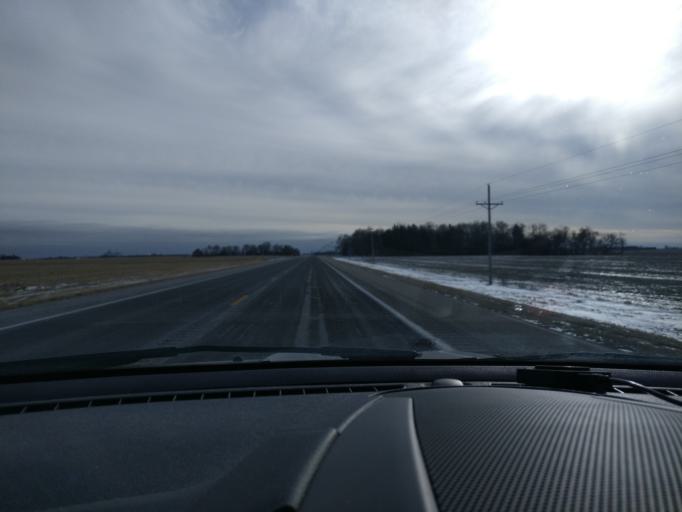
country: US
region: Nebraska
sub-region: Saunders County
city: Yutan
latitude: 41.2660
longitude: -96.5035
